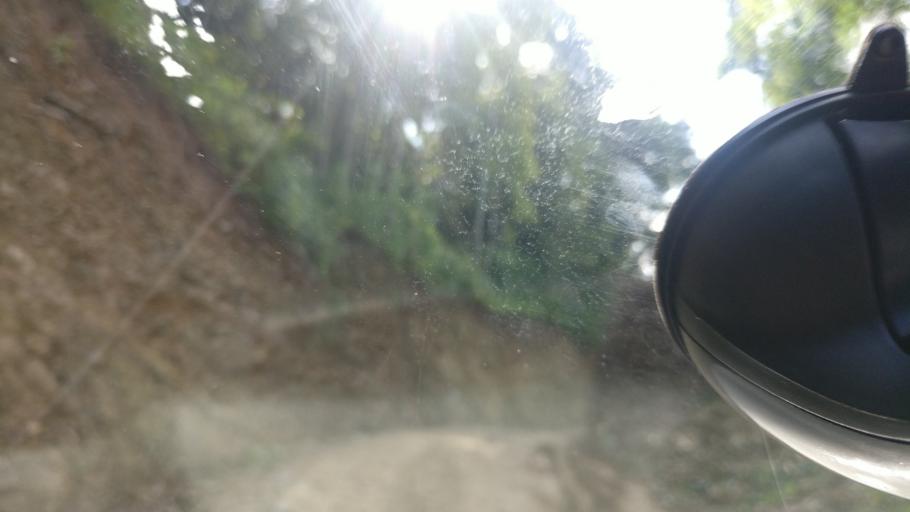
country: NP
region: Western Region
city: Baglung
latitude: 28.1369
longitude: 83.6539
